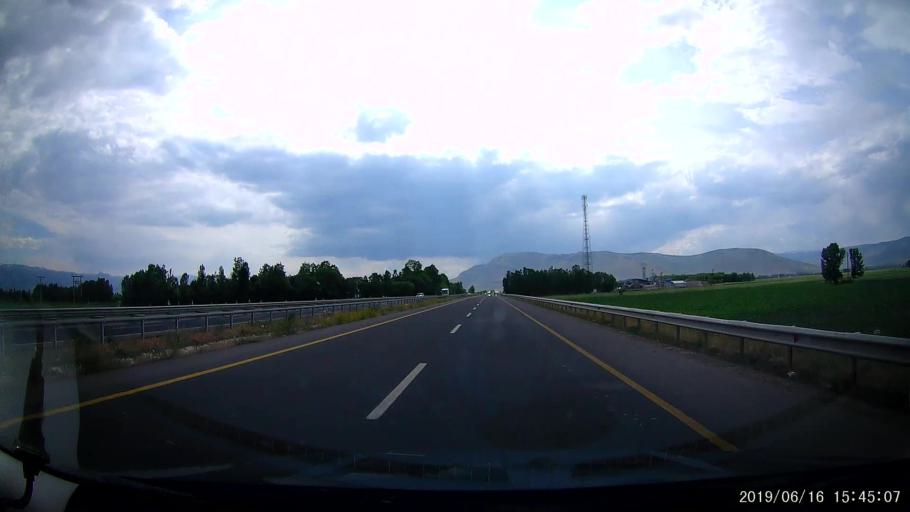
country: TR
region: Erzurum
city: Koprukoy
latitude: 39.9879
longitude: 41.7742
